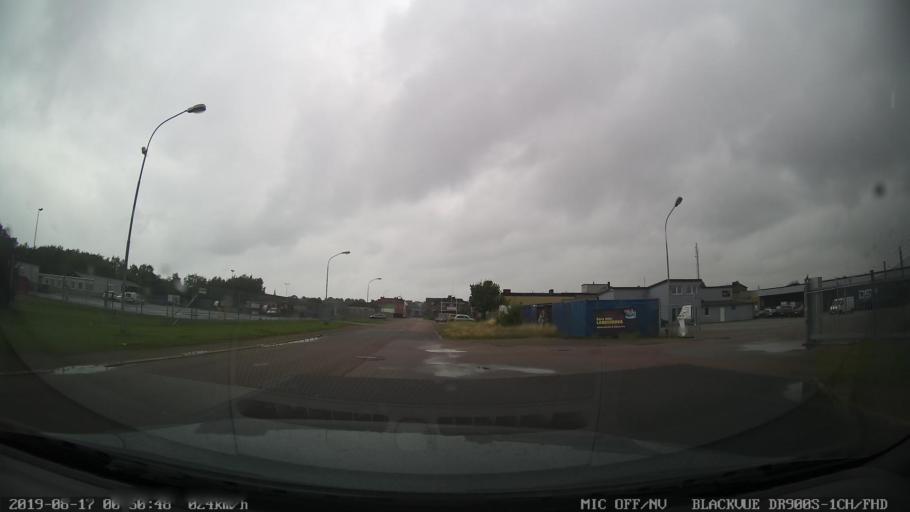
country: SE
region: Skane
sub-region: Landskrona
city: Landskrona
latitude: 55.8668
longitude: 12.8418
